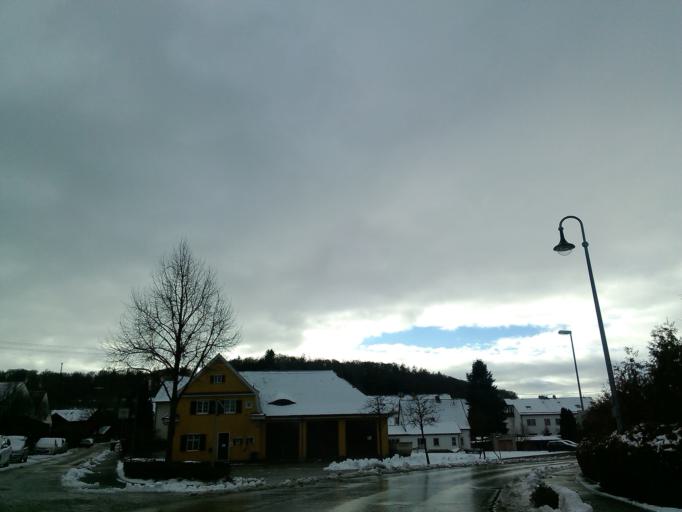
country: DE
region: Bavaria
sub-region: Swabia
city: Zusmarshausen
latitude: 48.3955
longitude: 10.5964
